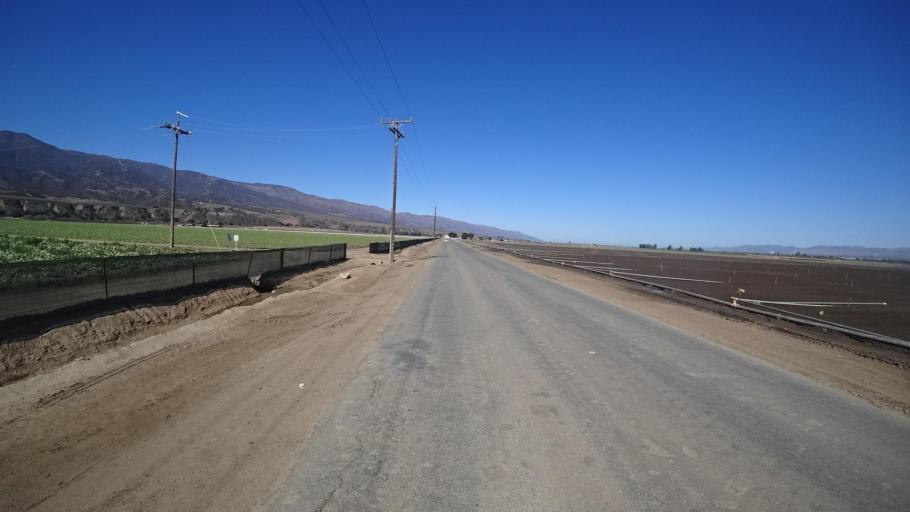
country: US
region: California
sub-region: Monterey County
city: Soledad
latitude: 36.4039
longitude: -121.3646
